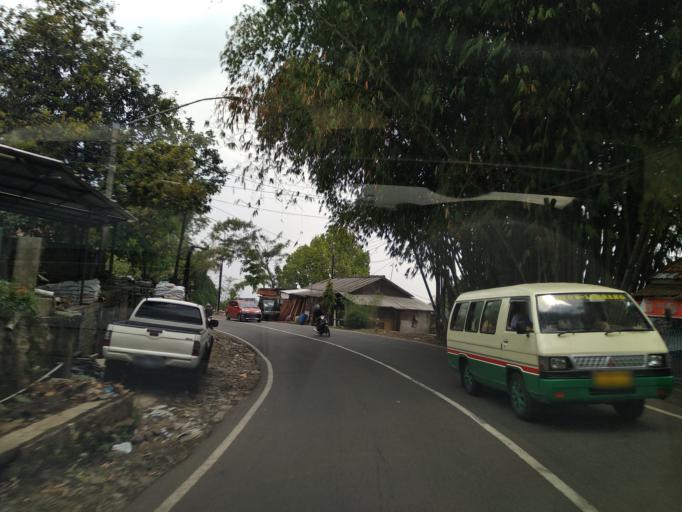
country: ID
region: West Java
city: Lembang
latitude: -6.8365
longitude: 107.5993
